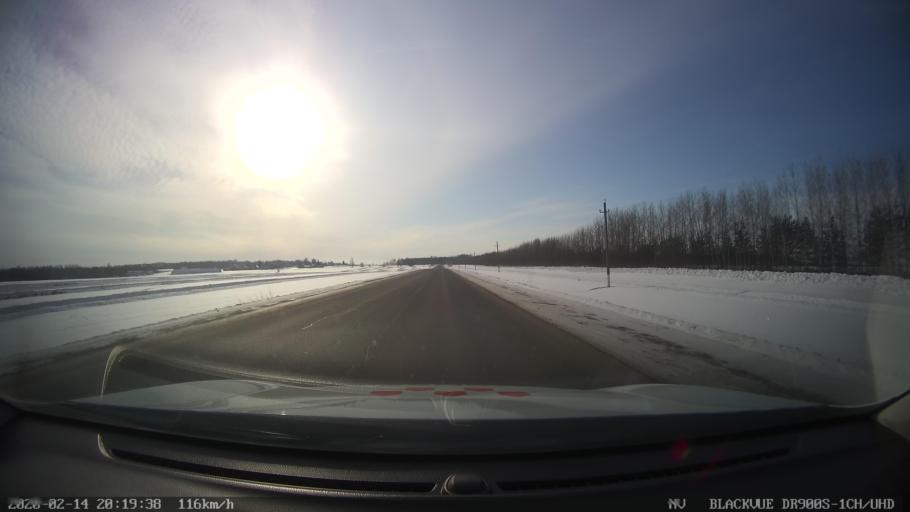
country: RU
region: Tatarstan
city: Verkhniy Uslon
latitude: 55.5682
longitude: 48.9013
